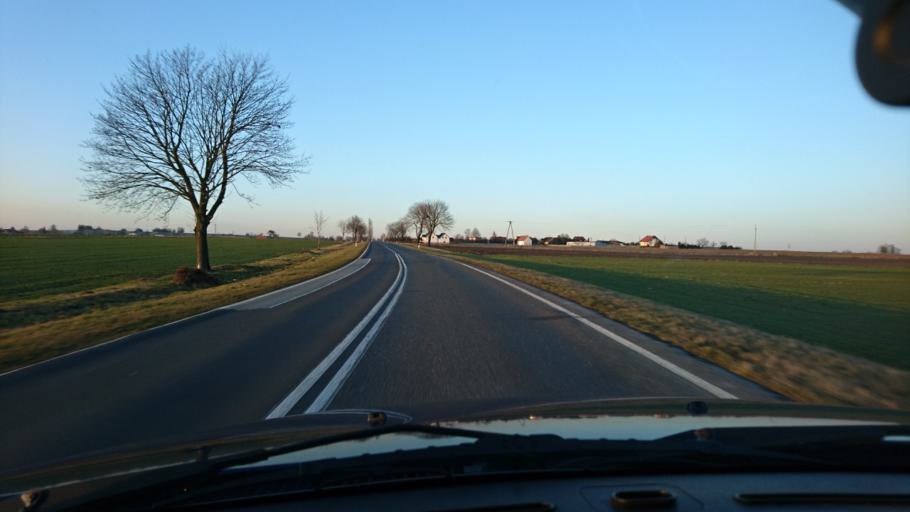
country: PL
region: Silesian Voivodeship
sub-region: Powiat gliwicki
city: Wielowies
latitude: 50.4654
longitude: 18.6110
